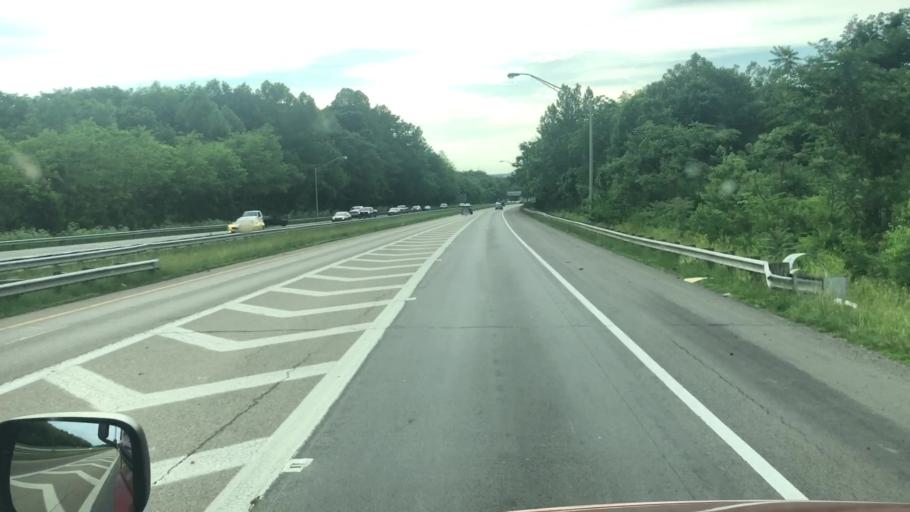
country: US
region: Ohio
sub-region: Greene County
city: Xenia
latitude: 39.6946
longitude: -83.9817
